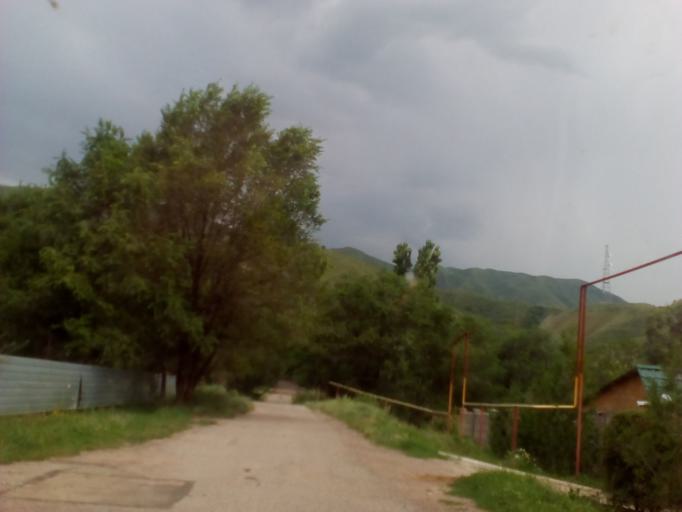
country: KZ
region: Almaty Oblysy
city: Burunday
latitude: 43.1585
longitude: 76.3975
